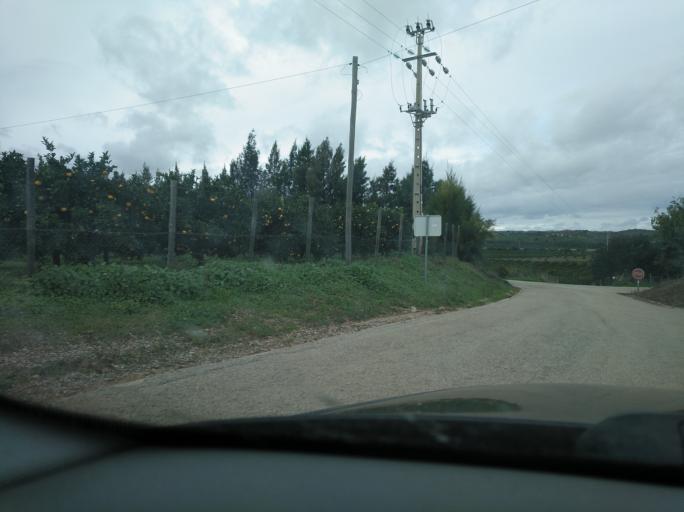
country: PT
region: Faro
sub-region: Vila Real de Santo Antonio
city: Monte Gordo
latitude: 37.1932
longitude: -7.5061
